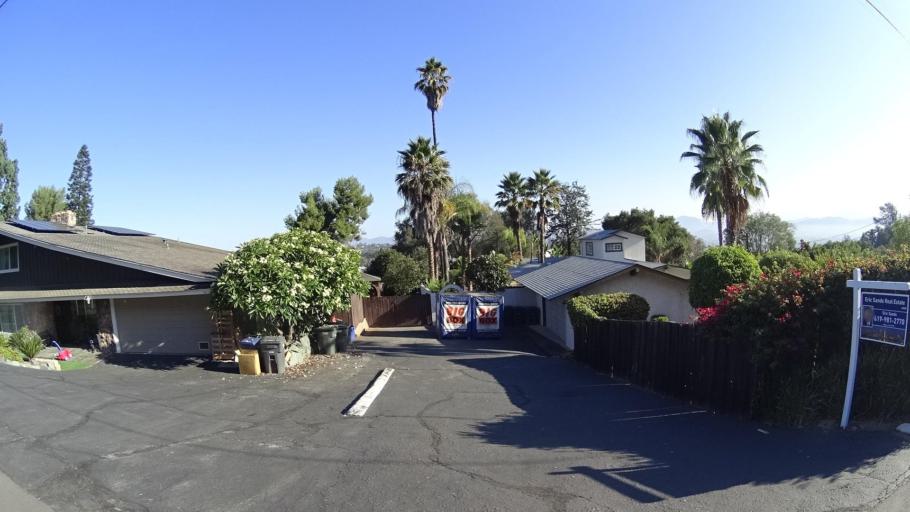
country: US
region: California
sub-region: San Diego County
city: Casa de Oro-Mount Helix
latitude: 32.7771
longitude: -116.9901
